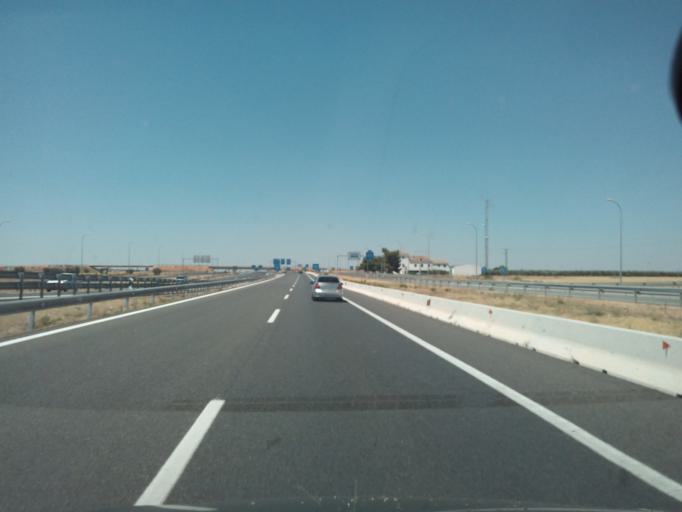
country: ES
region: Castille-La Mancha
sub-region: Province of Toledo
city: Dosbarrios
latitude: 39.9107
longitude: -3.4756
